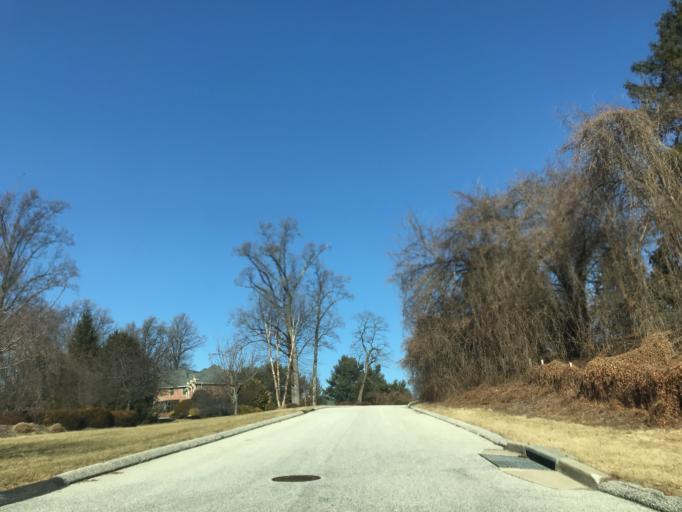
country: US
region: Maryland
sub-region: Baltimore County
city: Mays Chapel
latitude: 39.4054
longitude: -76.6788
